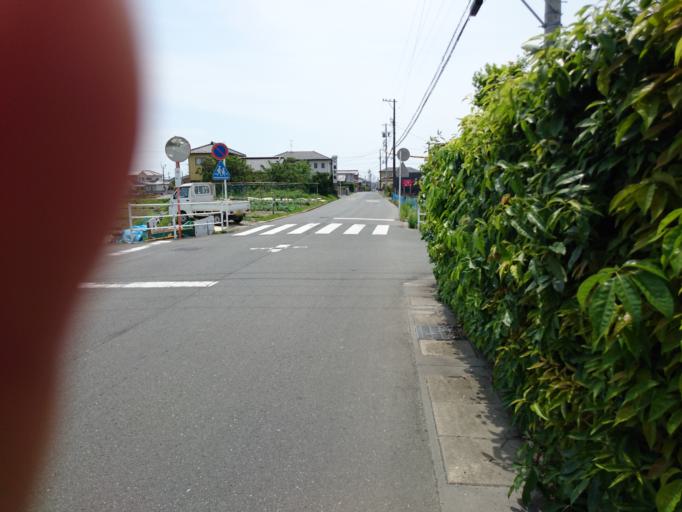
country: JP
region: Shizuoka
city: Hamakita
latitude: 34.7738
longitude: 137.7778
